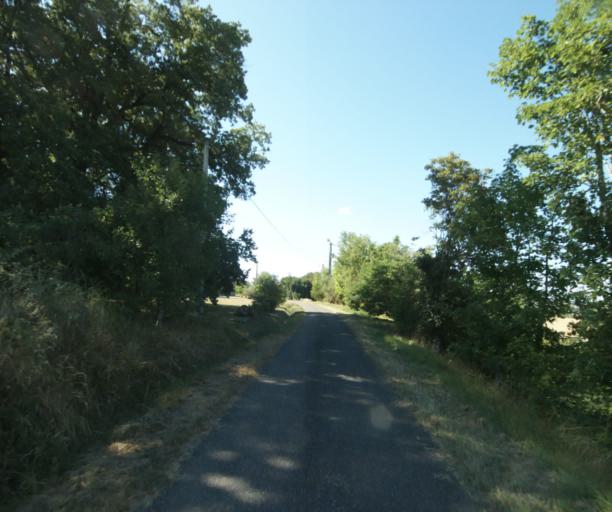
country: FR
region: Midi-Pyrenees
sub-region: Departement de la Haute-Garonne
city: Saint-Felix-Lauragais
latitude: 43.5241
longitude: 1.9066
